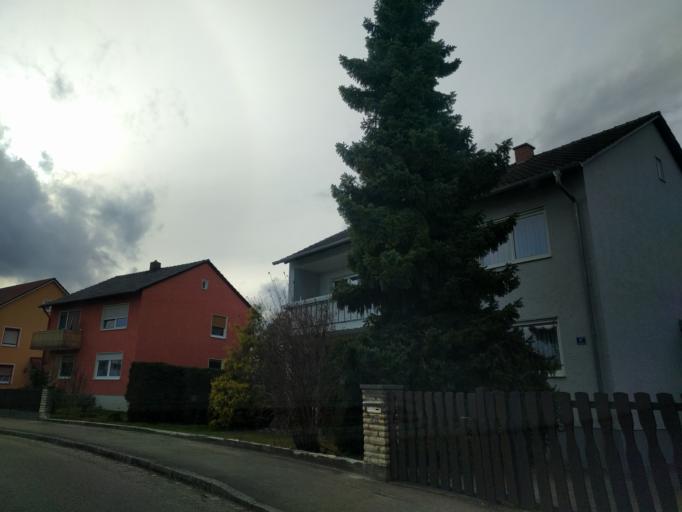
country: DE
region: Bavaria
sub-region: Swabia
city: Rain
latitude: 48.6948
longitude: 10.9159
